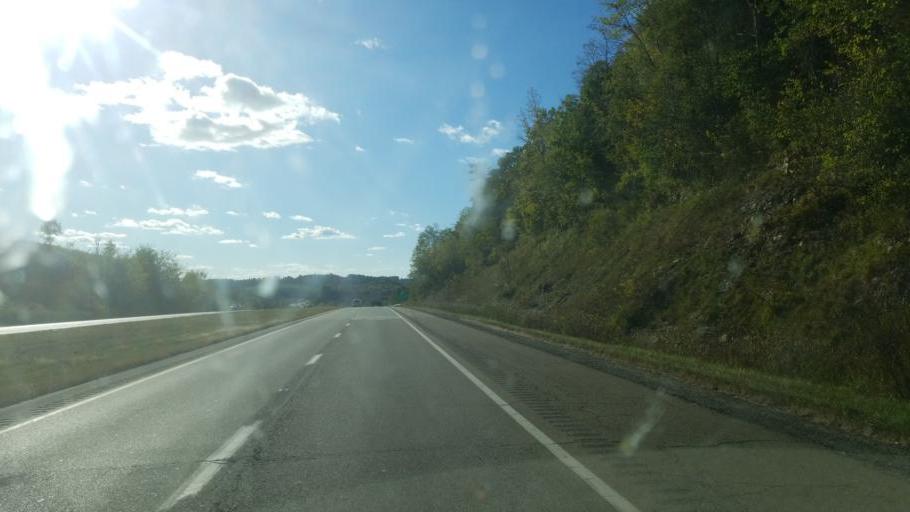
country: US
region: Ohio
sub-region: Belmont County
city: Bethesda
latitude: 40.0595
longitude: -81.1334
